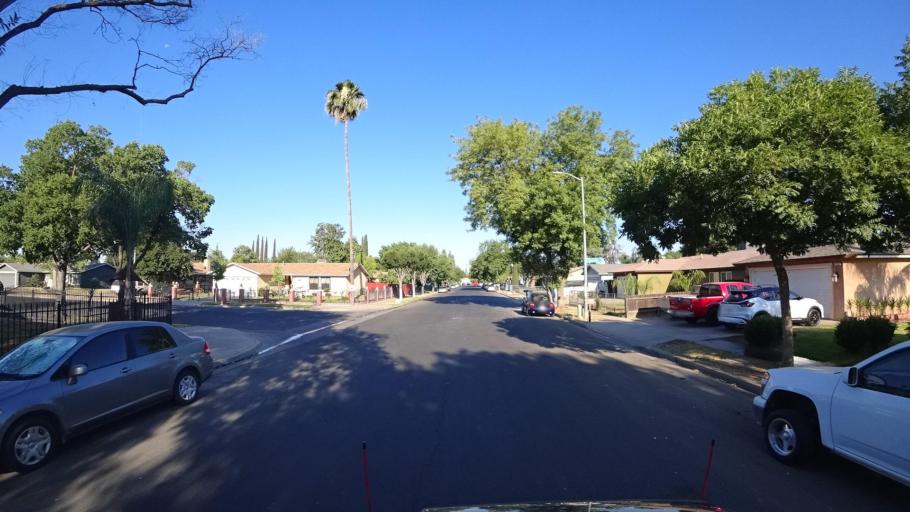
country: US
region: California
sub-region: Fresno County
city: Fresno
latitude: 36.7088
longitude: -119.7384
